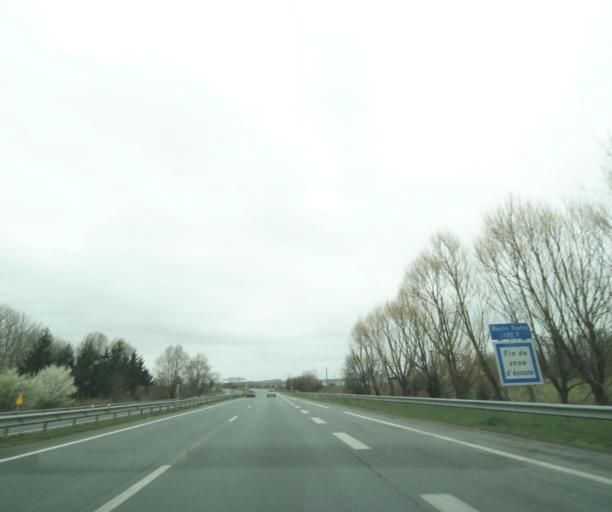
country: FR
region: Poitou-Charentes
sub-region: Departement de la Charente-Maritime
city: Breuil-Magne
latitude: 45.9714
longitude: -0.9859
